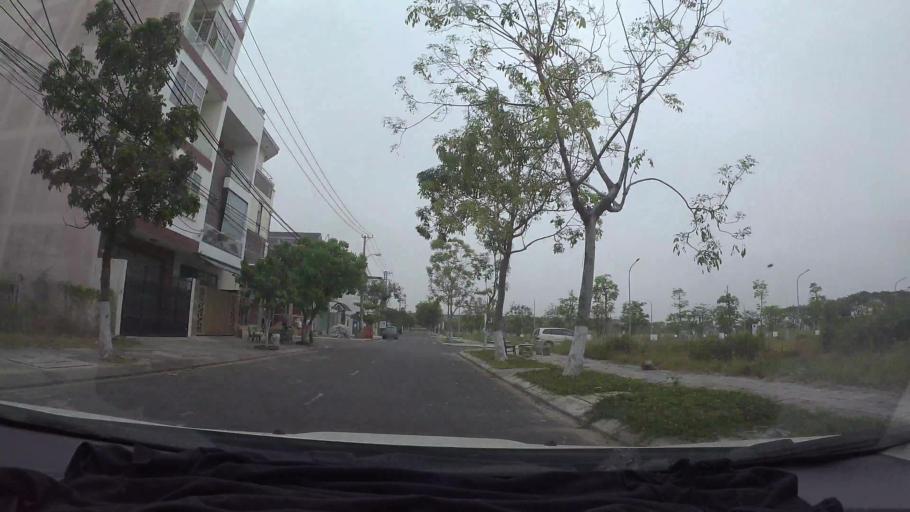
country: VN
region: Da Nang
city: Ngu Hanh Son
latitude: 16.0321
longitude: 108.2319
